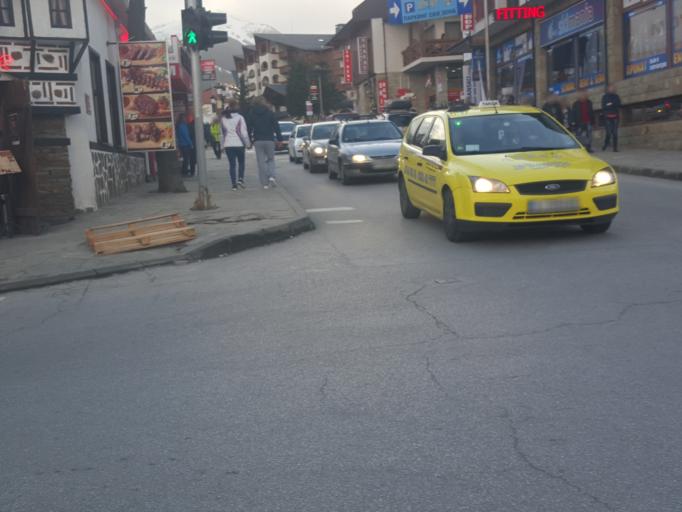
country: BG
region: Blagoevgrad
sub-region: Obshtina Bansko
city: Bansko
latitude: 41.8279
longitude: 23.4794
